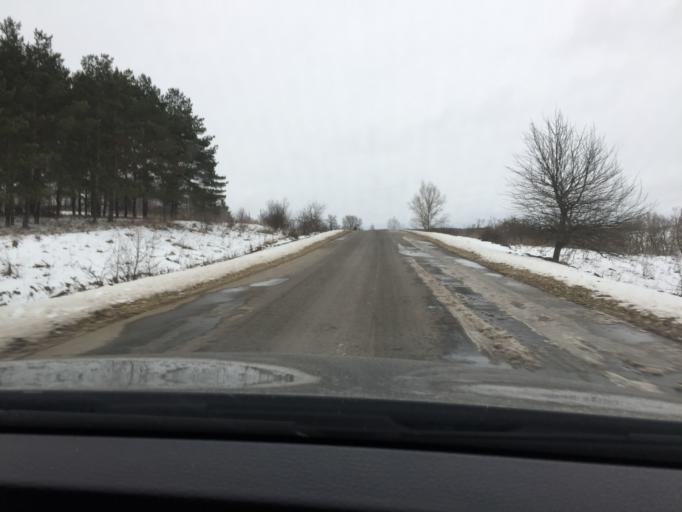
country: RU
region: Tula
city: Shchekino
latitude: 53.8294
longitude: 37.5602
